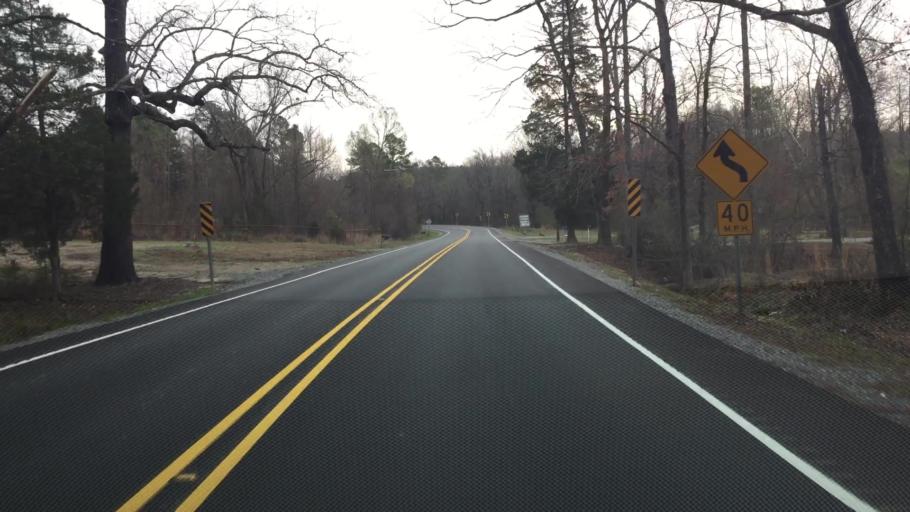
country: US
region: Arkansas
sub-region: Saline County
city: Haskell
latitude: 34.6121
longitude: -92.7982
